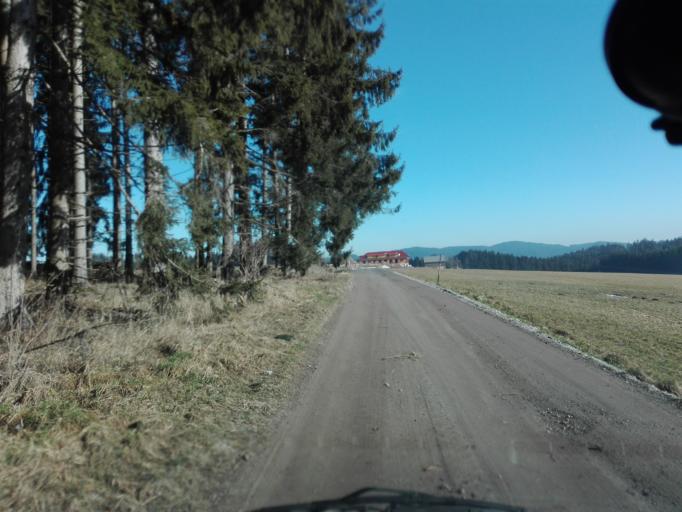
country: AT
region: Upper Austria
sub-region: Politischer Bezirk Urfahr-Umgebung
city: Sonnberg im Muehlkreis
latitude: 48.4614
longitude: 14.3204
